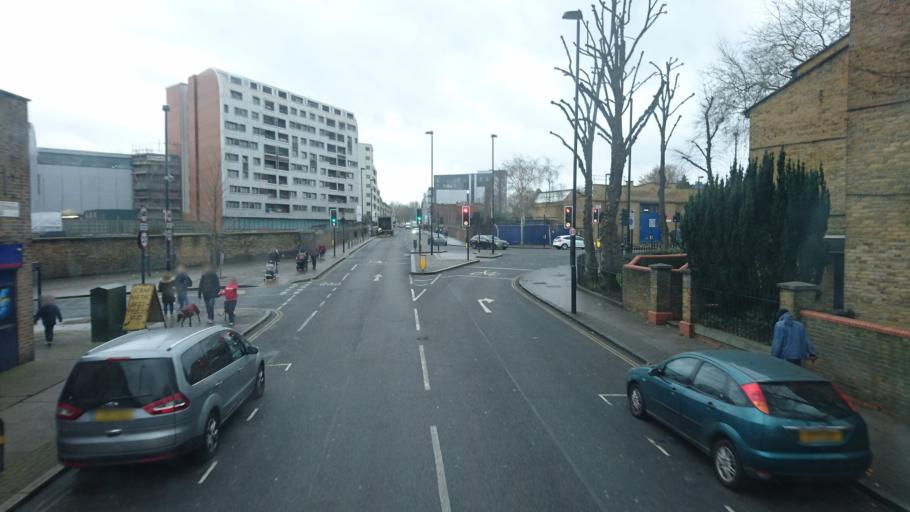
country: GB
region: England
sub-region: Greater London
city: Holloway
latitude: 51.5505
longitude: -0.1180
